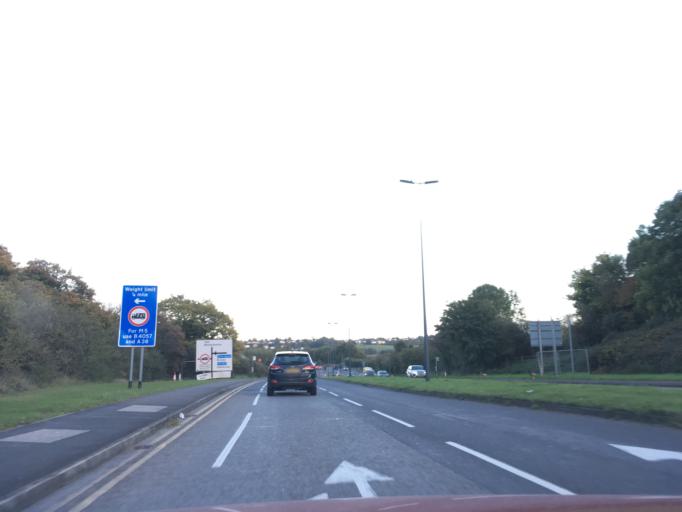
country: GB
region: England
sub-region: South Gloucestershire
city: Stoke Gifford
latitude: 51.5215
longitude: -2.5305
